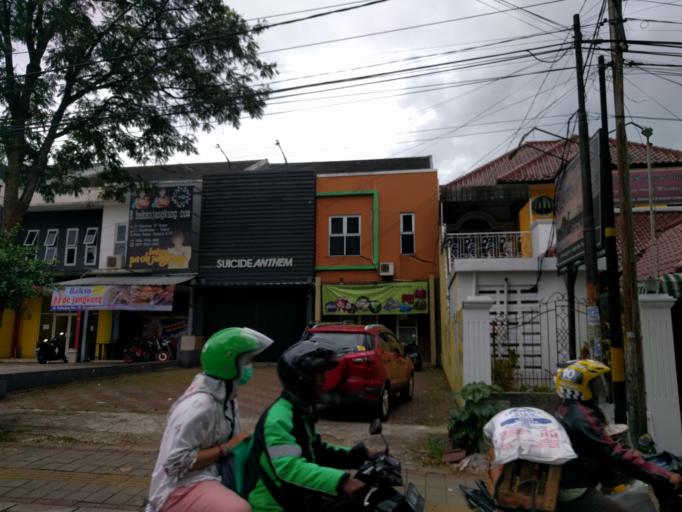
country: ID
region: West Java
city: Bogor
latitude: -6.5913
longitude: 106.8067
